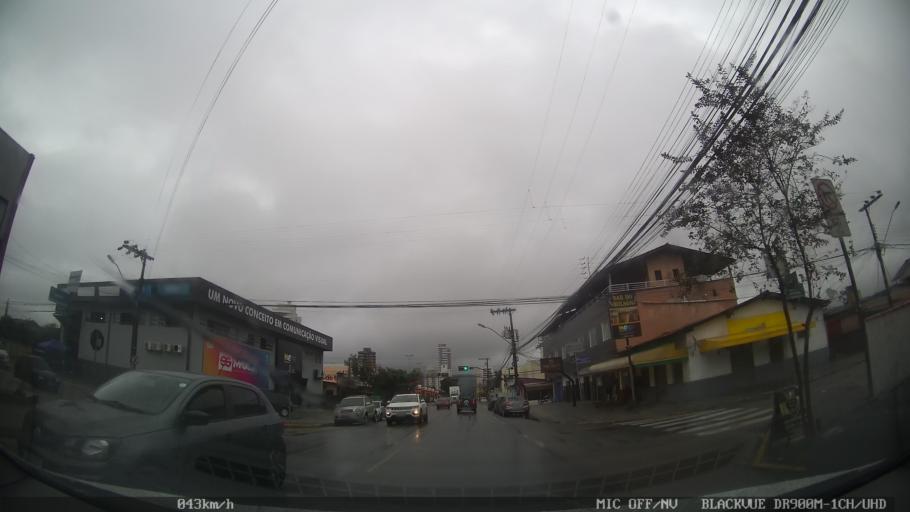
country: BR
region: Santa Catarina
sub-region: Itajai
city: Itajai
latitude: -26.9052
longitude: -48.6777
